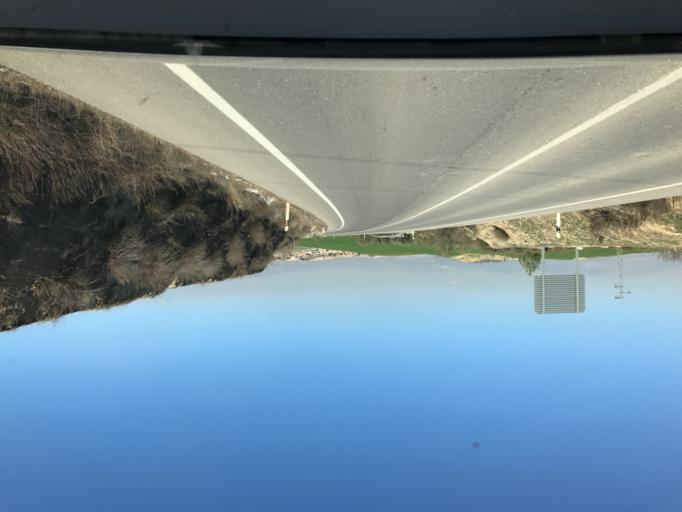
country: ES
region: Andalusia
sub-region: Provincia de Granada
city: Otura
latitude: 37.0772
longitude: -3.6615
